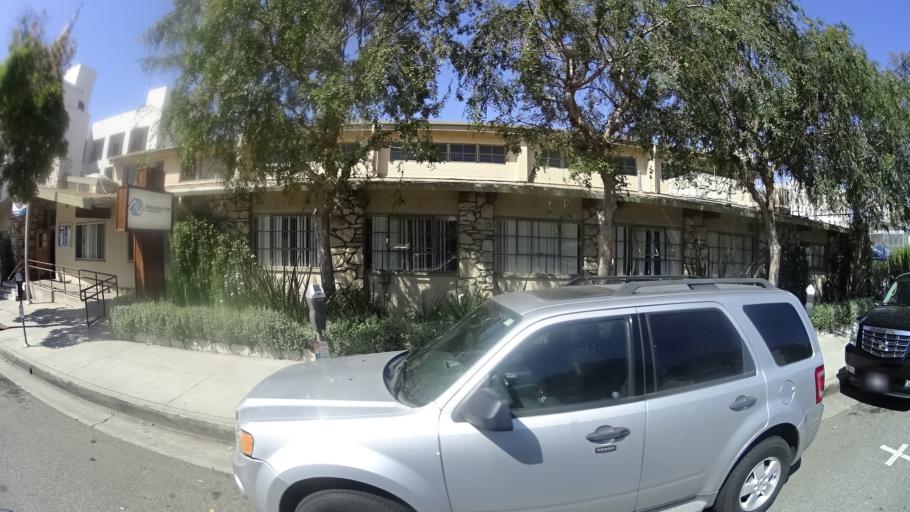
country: US
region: California
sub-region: Los Angeles County
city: Santa Monica
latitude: 34.0214
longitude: -118.4937
